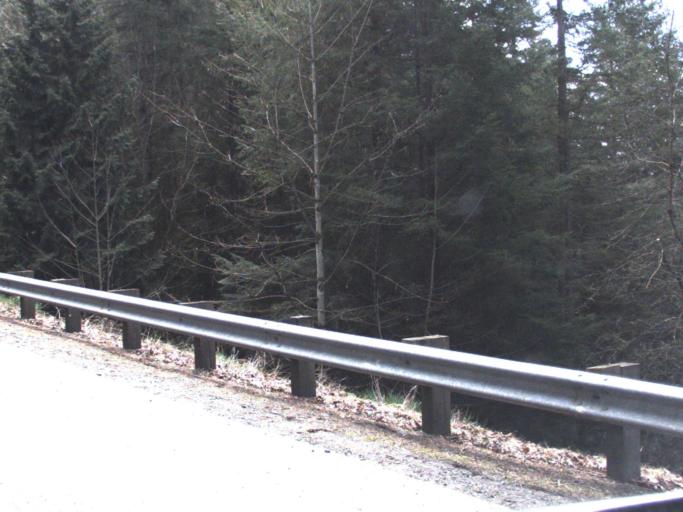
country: US
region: Washington
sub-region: King County
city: Black Diamond
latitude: 47.3332
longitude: -122.0117
